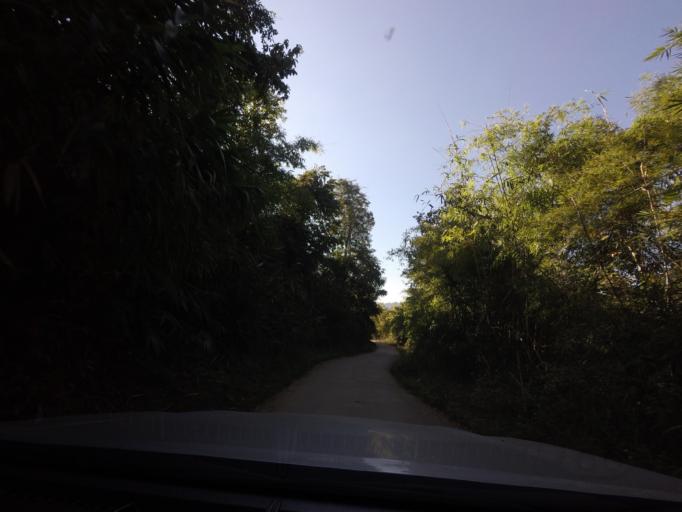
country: TH
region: Lampang
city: Chae Hom
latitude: 18.6089
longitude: 99.6411
